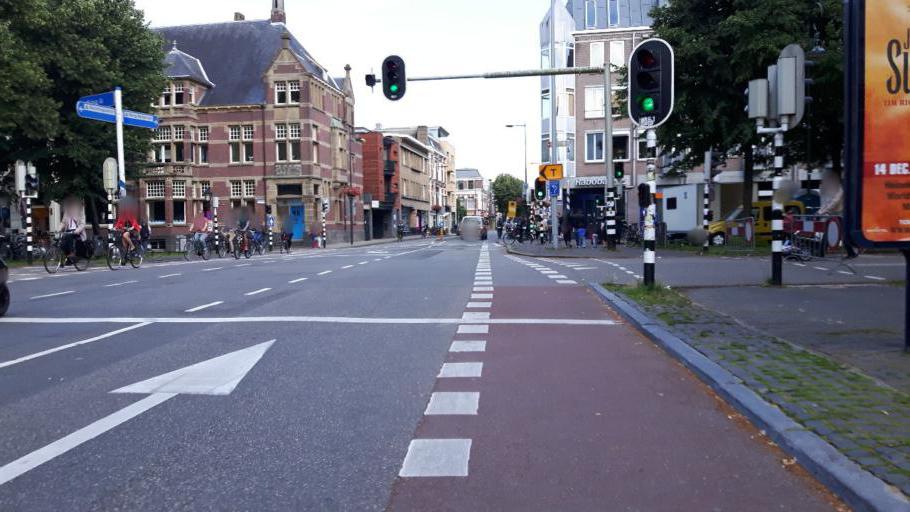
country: NL
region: Utrecht
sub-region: Gemeente Utrecht
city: Utrecht
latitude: 52.0911
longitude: 5.1328
